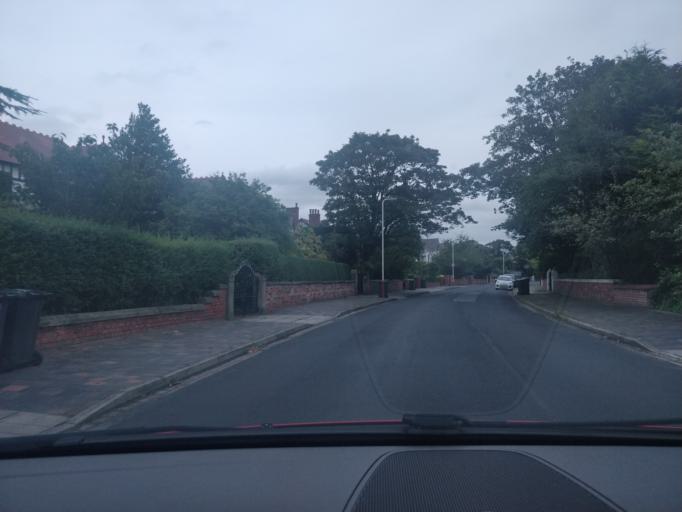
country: GB
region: England
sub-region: Sefton
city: Southport
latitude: 53.6349
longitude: -3.0307
